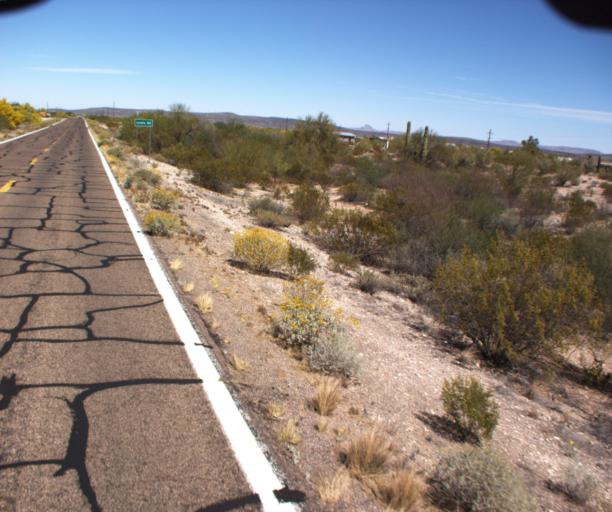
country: US
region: Arizona
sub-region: Pima County
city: Ajo
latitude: 32.4206
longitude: -112.8715
